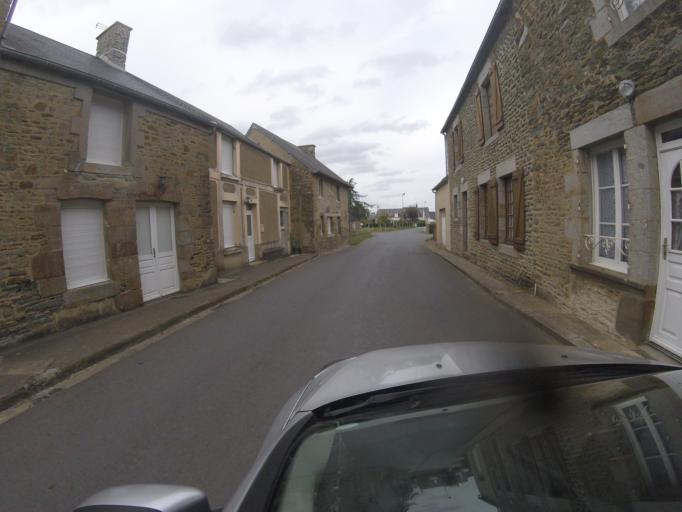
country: FR
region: Lower Normandy
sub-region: Departement de la Manche
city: Le Val-Saint-Pere
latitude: 48.6319
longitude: -1.3874
